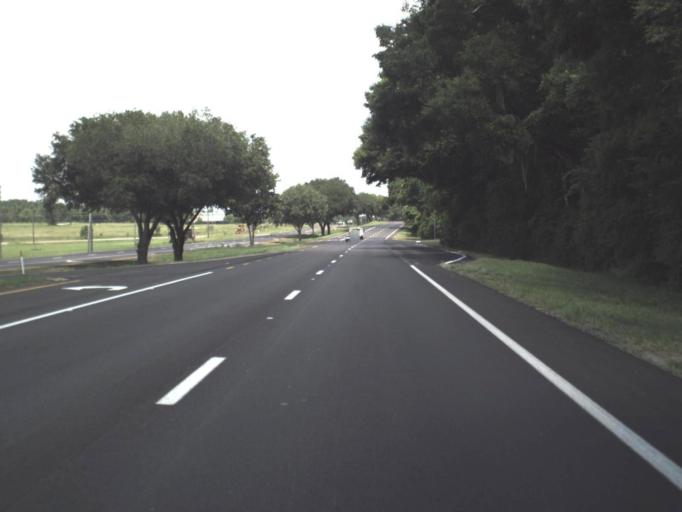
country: US
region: Florida
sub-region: Alachua County
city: Alachua
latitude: 29.7770
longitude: -82.4464
